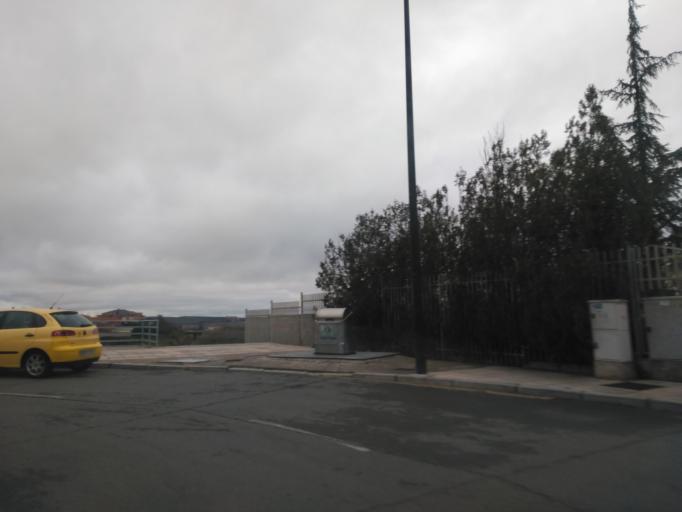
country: ES
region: Castille and Leon
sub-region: Provincia de Salamanca
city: Salamanca
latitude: 40.9524
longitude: -5.6736
